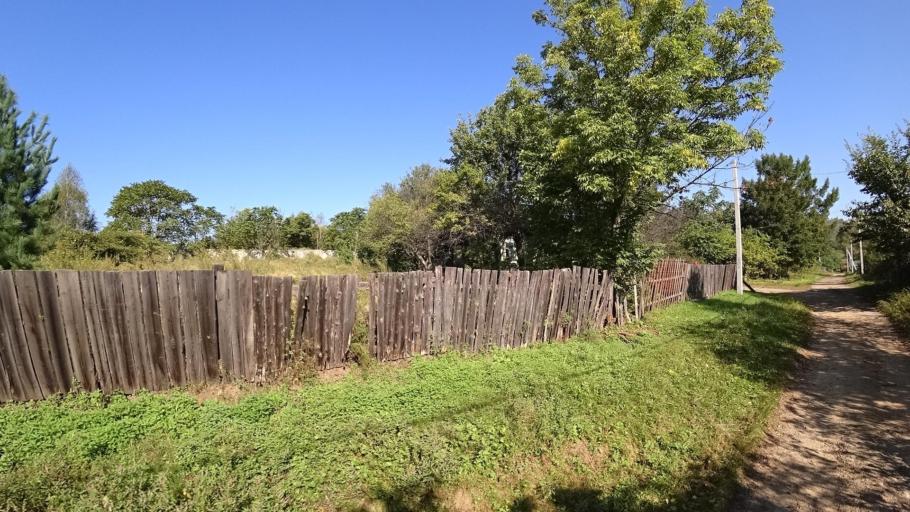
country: RU
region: Jewish Autonomous Oblast
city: Bira
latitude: 49.0034
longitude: 132.4606
